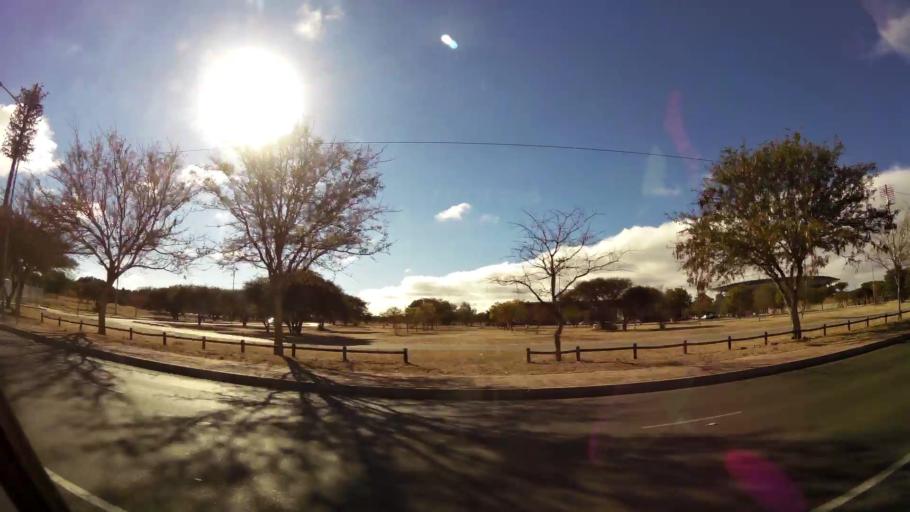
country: ZA
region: Limpopo
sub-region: Capricorn District Municipality
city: Polokwane
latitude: -23.9220
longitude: 29.4629
